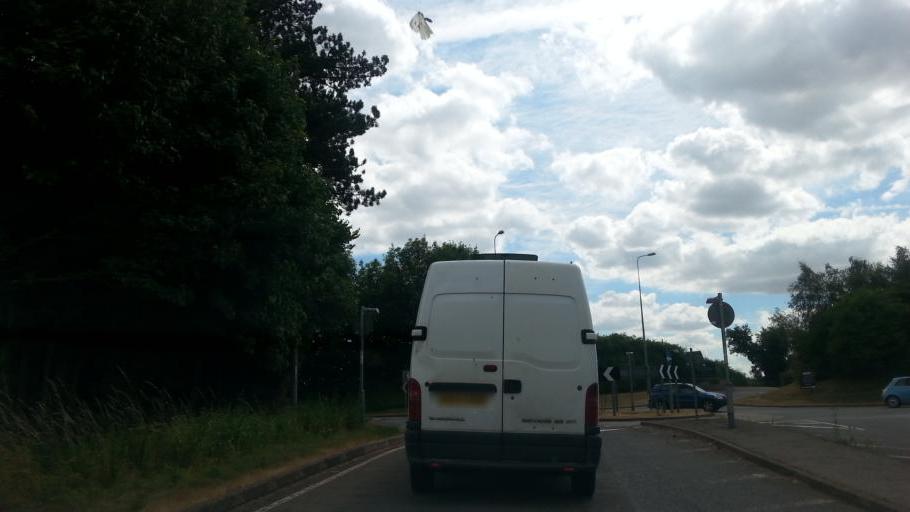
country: GB
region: England
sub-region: Northamptonshire
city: Towcester
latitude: 52.1083
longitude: -1.0022
